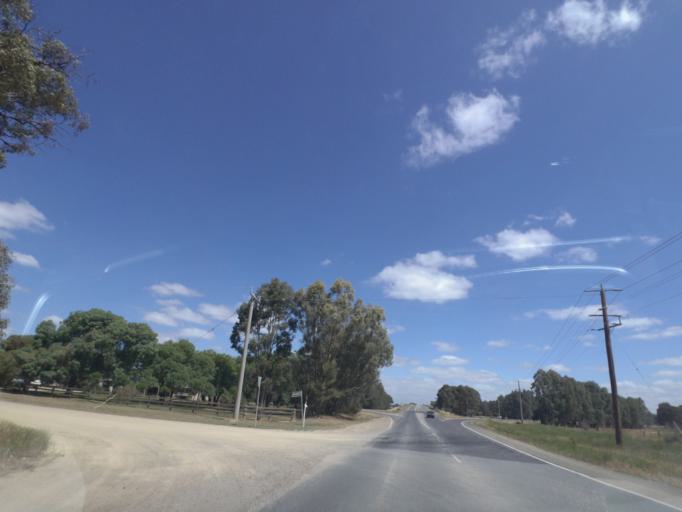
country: AU
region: Victoria
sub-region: Wangaratta
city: Wangaratta
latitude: -36.4007
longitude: 146.2988
